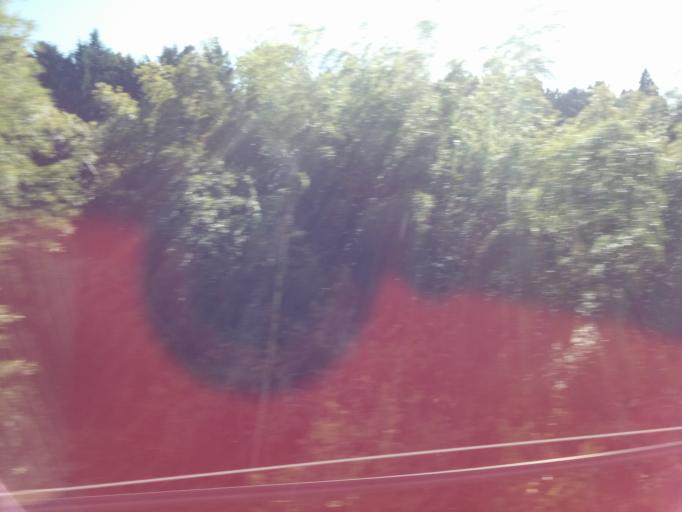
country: JP
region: Gifu
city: Tarui
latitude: 35.3614
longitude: 136.4806
